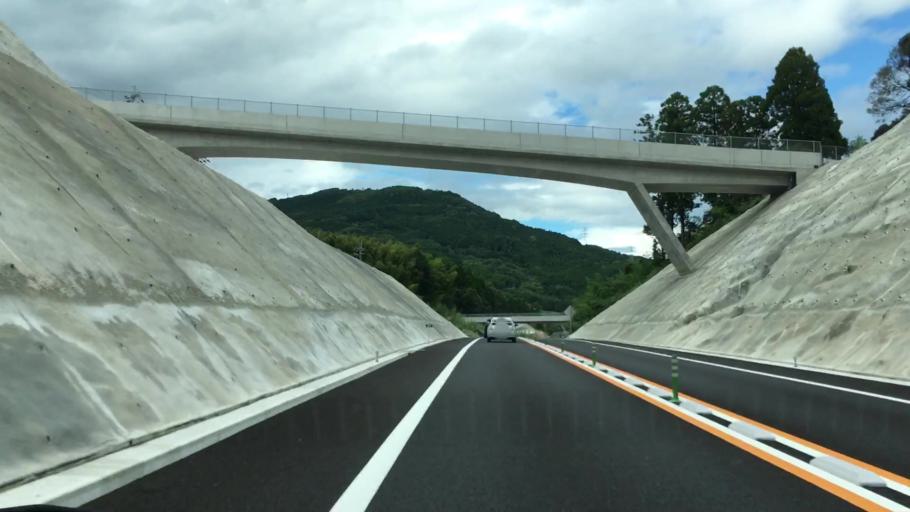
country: JP
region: Saga Prefecture
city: Imaricho-ko
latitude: 33.3067
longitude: 129.9161
